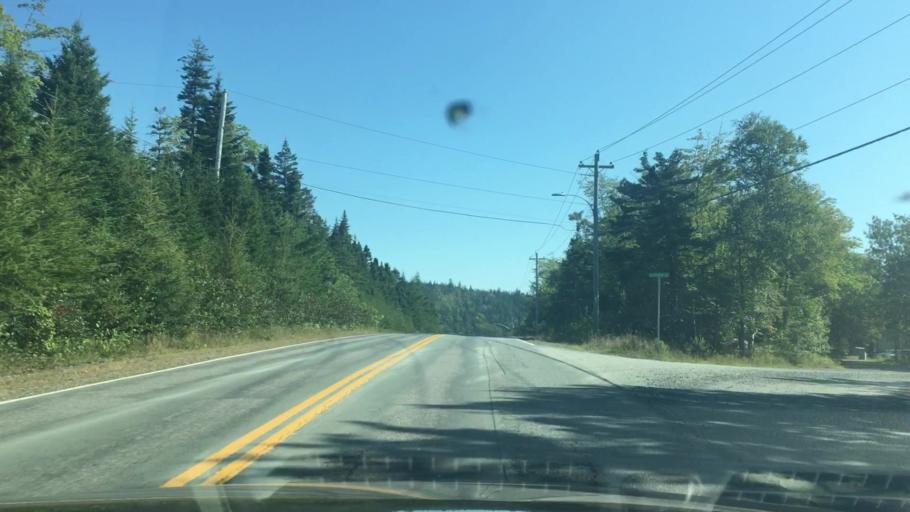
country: CA
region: Nova Scotia
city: Cole Harbour
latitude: 44.7770
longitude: -63.0463
